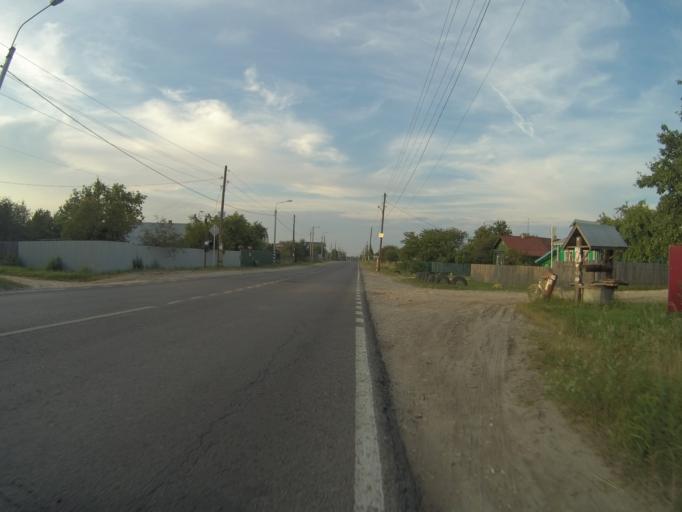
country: RU
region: Vladimir
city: Raduzhnyy
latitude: 56.0142
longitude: 40.3117
